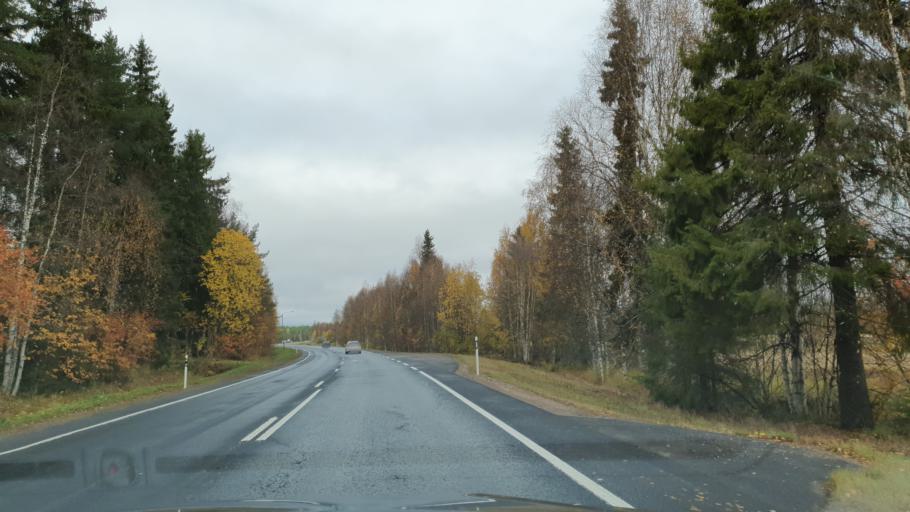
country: FI
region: Lapland
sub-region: Rovaniemi
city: Rovaniemi
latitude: 66.6336
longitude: 25.5109
